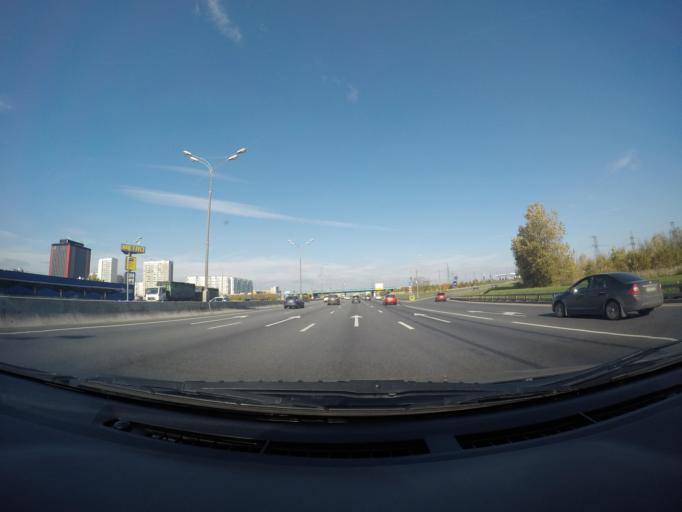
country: RU
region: Moscow
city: Gol'yanovo
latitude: 55.8107
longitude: 37.8384
